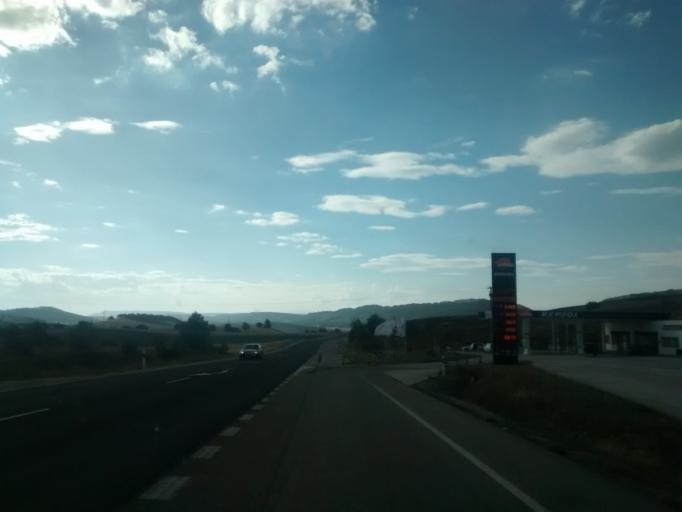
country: ES
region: Castille and Leon
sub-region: Provincia de Burgos
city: Basconcillos del Tozo
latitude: 42.6930
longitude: -3.9795
